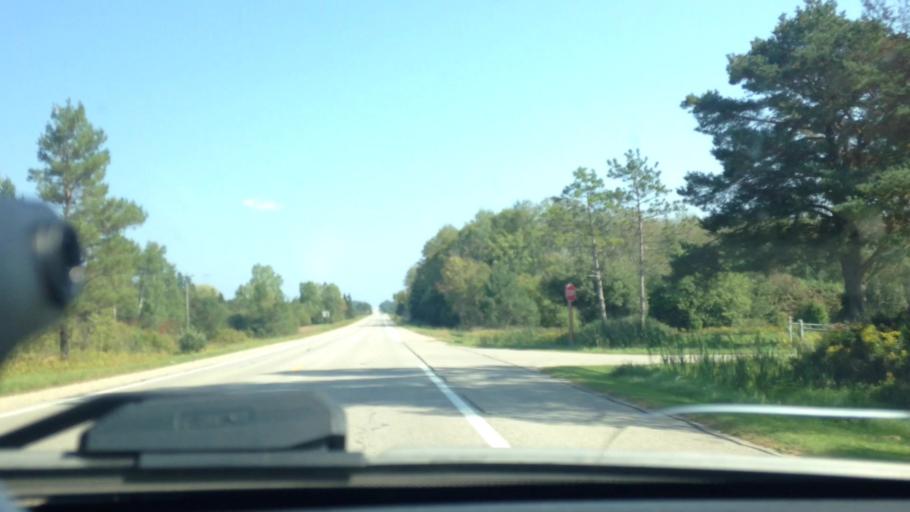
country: US
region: Michigan
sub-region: Luce County
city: Newberry
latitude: 46.3105
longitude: -85.5903
